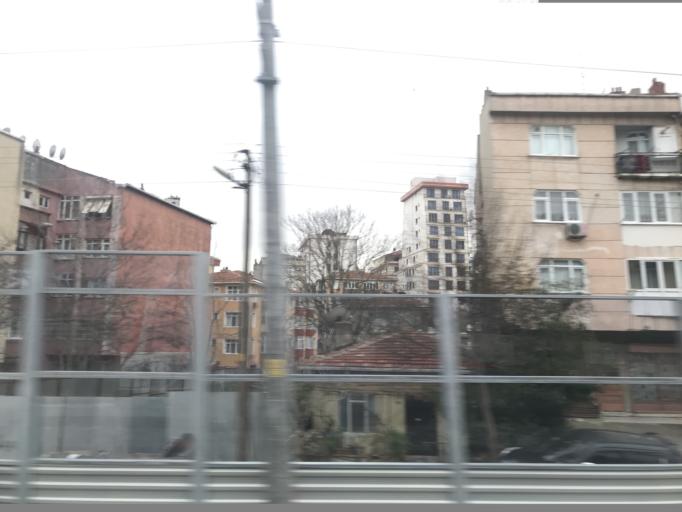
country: TR
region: Istanbul
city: Mahmutbey
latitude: 40.9958
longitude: 28.7677
